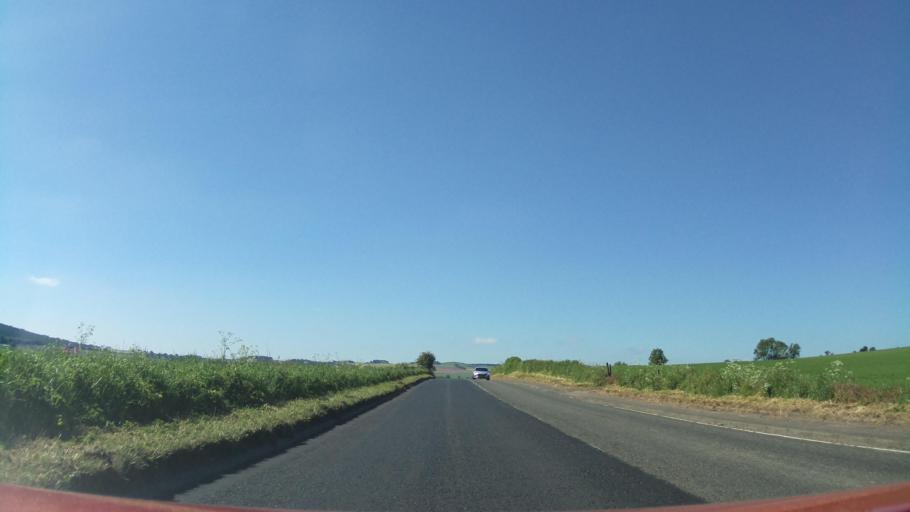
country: GB
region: Scotland
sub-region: Fife
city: Ceres
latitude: 56.3320
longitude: -2.9755
